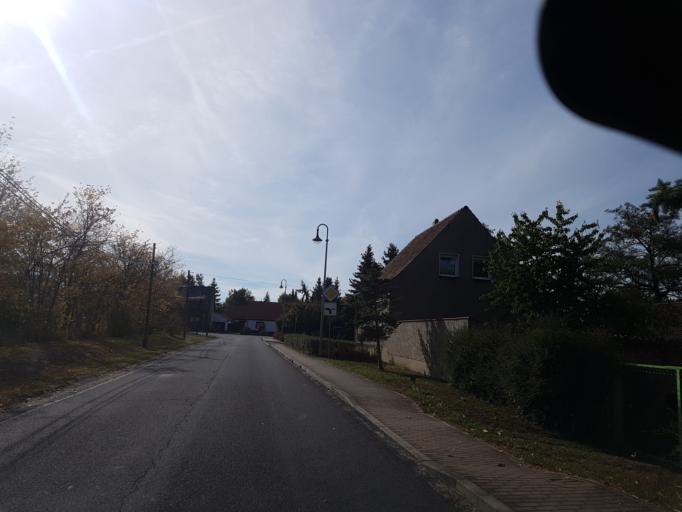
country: DE
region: Brandenburg
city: Schlieben
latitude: 51.7018
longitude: 13.4141
